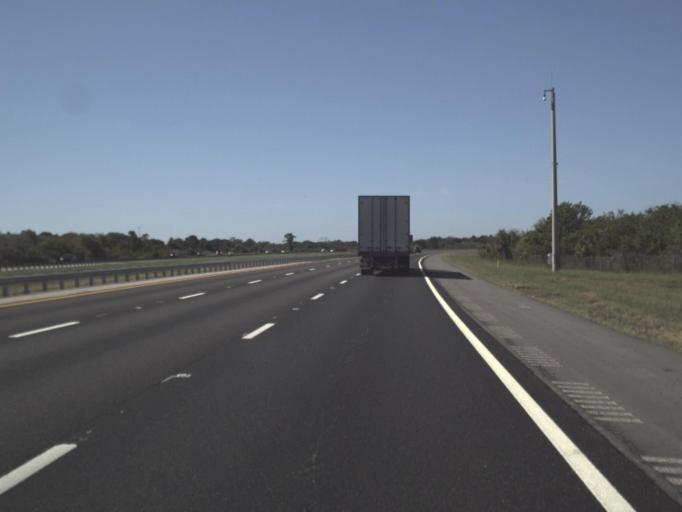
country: US
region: Florida
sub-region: Lee County
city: Suncoast Estates
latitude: 26.7235
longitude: -81.8266
